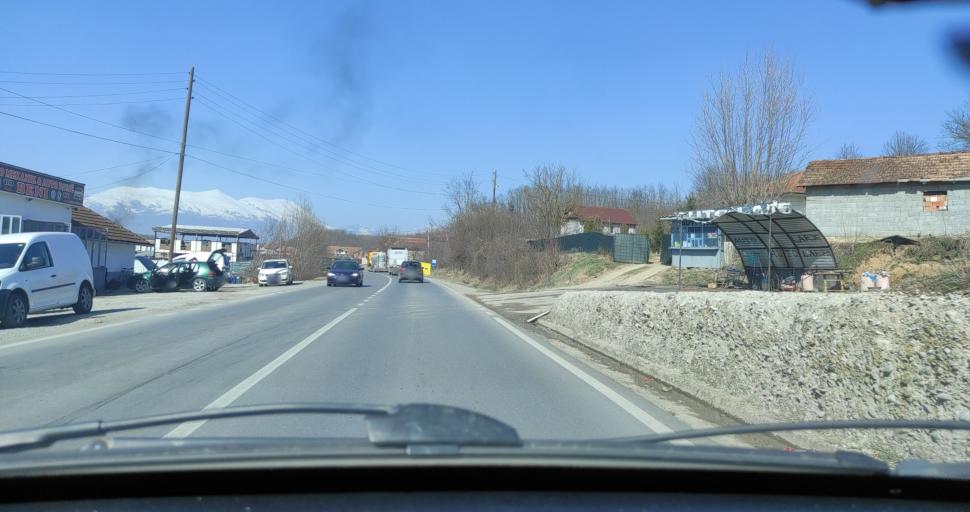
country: XK
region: Pec
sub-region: Komuna e Pejes
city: Kosuriq
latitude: 42.6346
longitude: 20.4476
